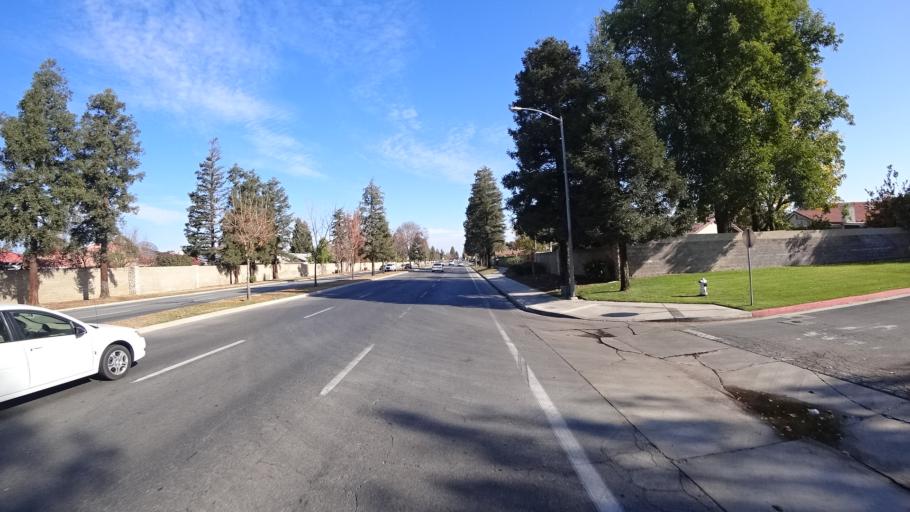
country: US
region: California
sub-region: Kern County
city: Greenacres
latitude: 35.4014
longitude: -119.0901
